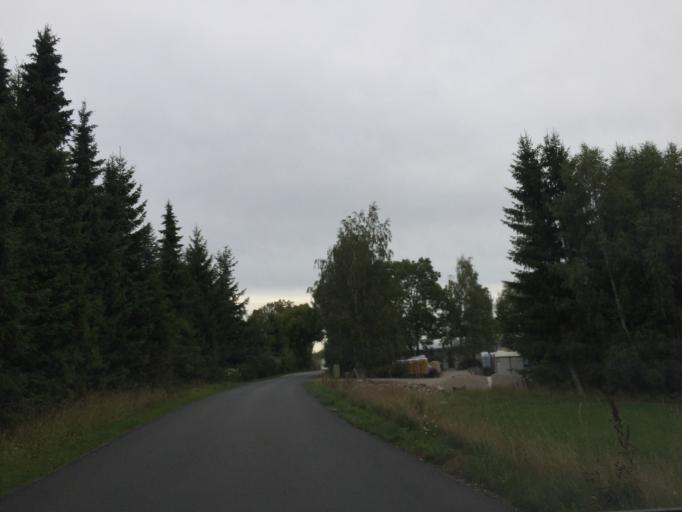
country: NO
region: Ostfold
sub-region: Hvaler
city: Skjaerhalden
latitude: 59.0613
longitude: 11.0335
